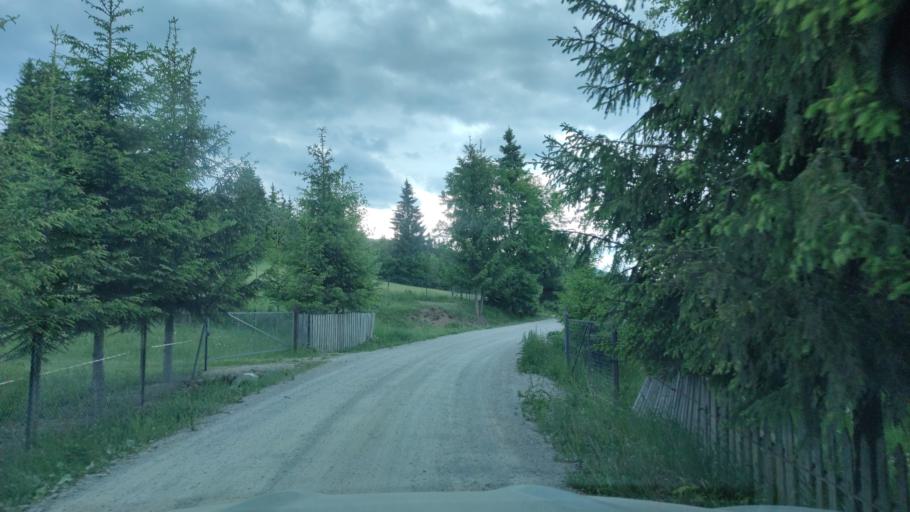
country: RO
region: Harghita
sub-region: Comuna Joseni
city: Joseni
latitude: 46.6648
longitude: 25.3836
